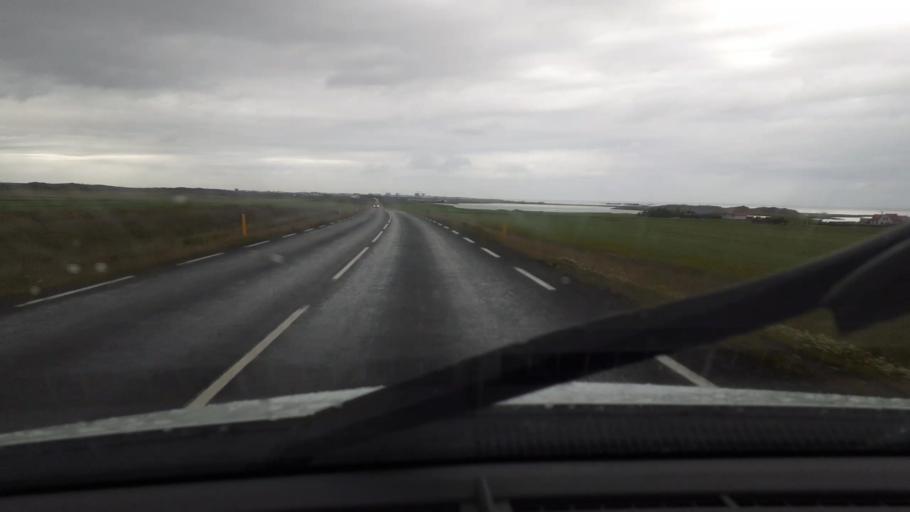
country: IS
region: West
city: Akranes
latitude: 64.3551
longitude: -21.9867
